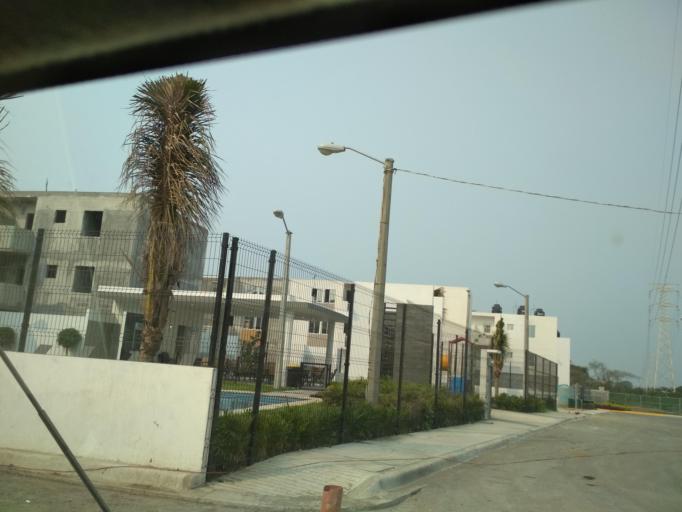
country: MX
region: Veracruz
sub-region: Veracruz
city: Las Amapolas
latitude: 19.1521
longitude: -96.2327
